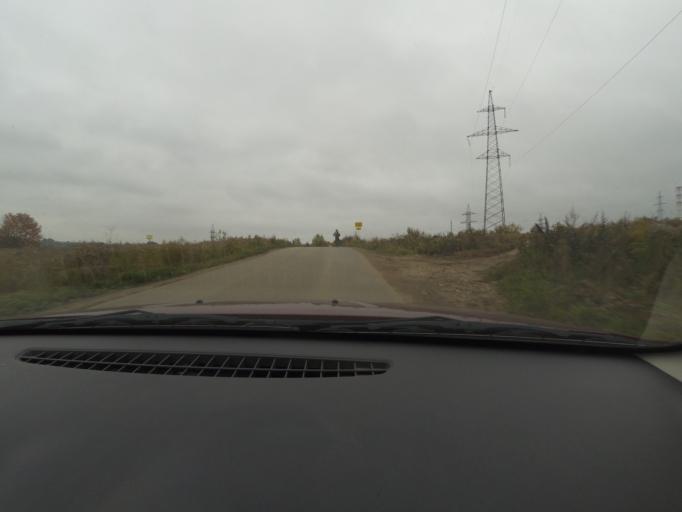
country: RU
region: Nizjnij Novgorod
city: Afonino
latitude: 56.2747
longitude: 44.0564
